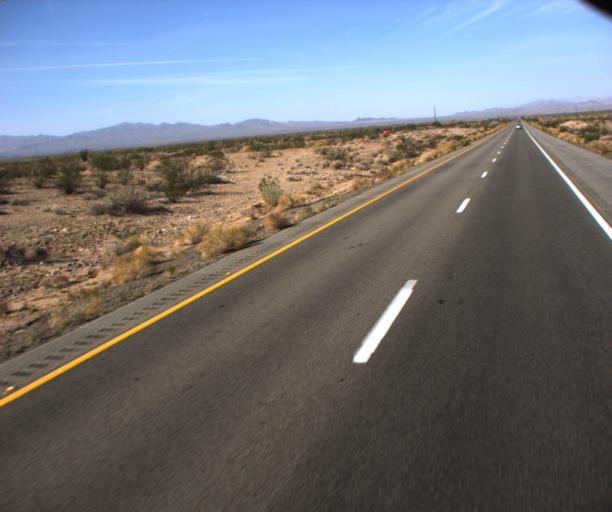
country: US
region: Arizona
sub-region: Mohave County
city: Desert Hills
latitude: 34.7870
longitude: -114.1720
